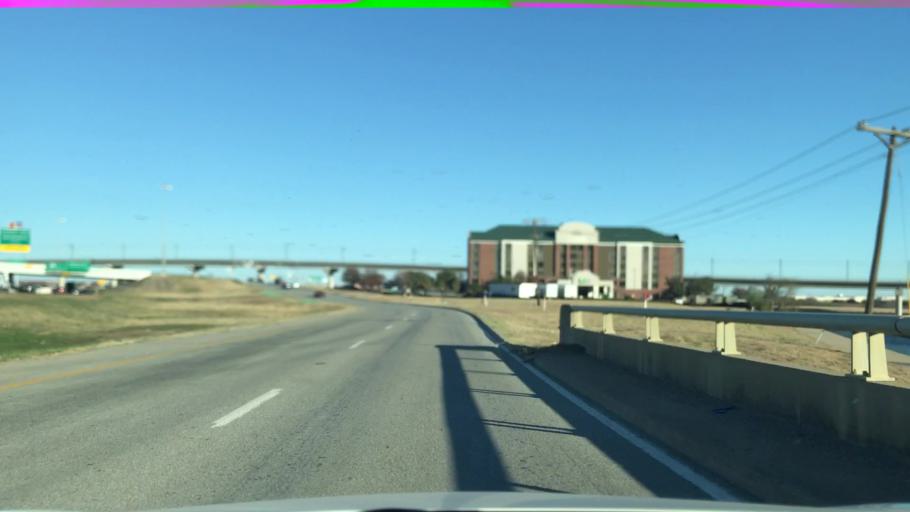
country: US
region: Texas
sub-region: Dallas County
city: Irving
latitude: 32.8773
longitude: -96.9459
